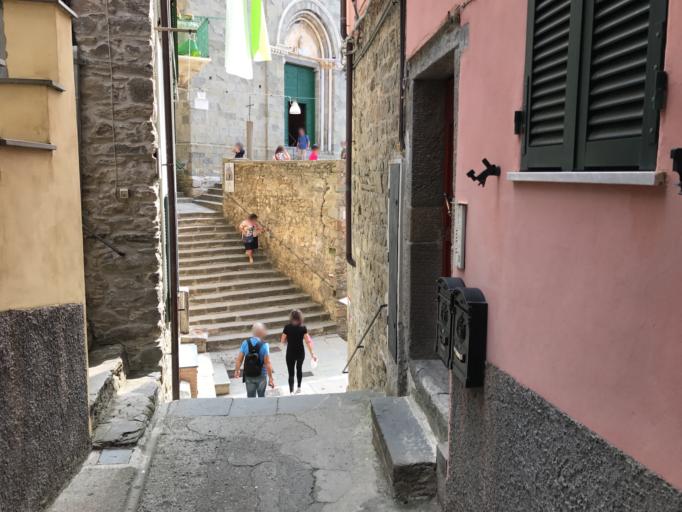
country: IT
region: Liguria
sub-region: Provincia di La Spezia
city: Vernazza
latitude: 44.1209
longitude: 9.7091
